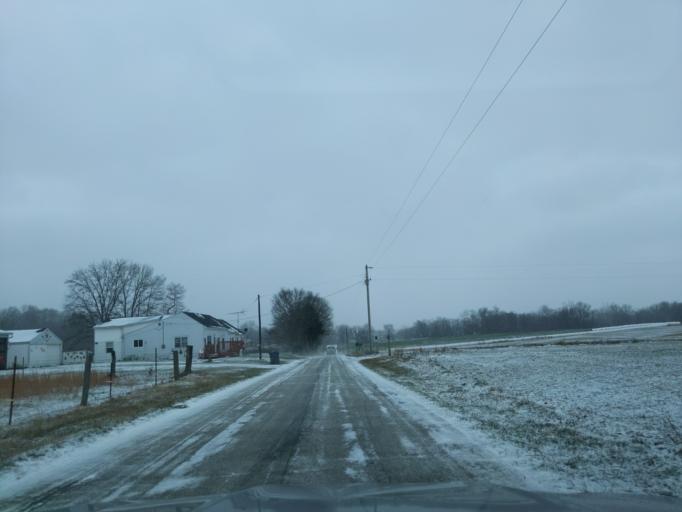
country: US
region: Indiana
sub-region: Decatur County
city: Westport
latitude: 39.2286
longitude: -85.5069
